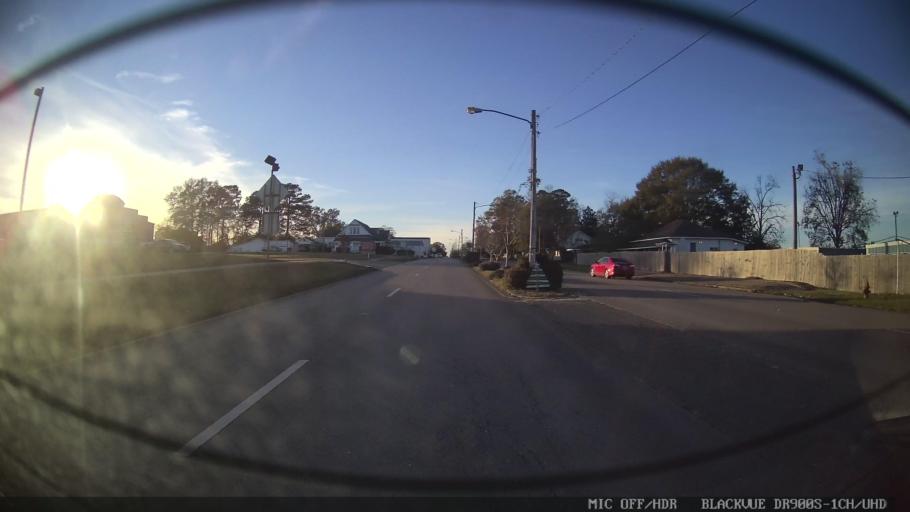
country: US
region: Mississippi
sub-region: Lamar County
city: Lumberton
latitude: 31.0002
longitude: -89.4488
